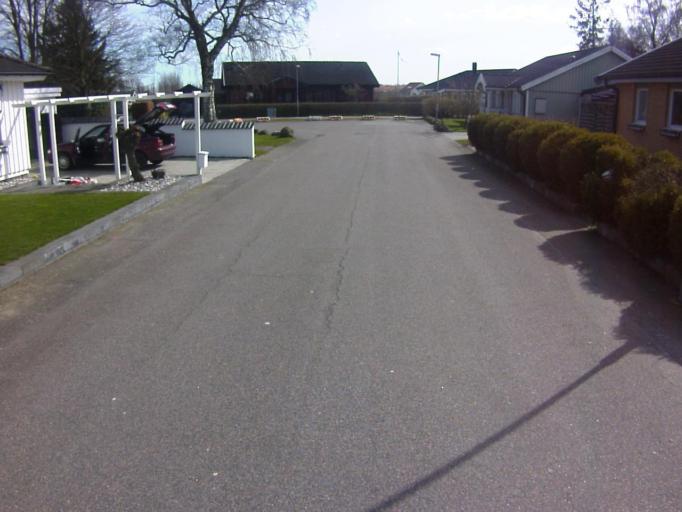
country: SE
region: Skane
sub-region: Kavlinge Kommun
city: Kaevlinge
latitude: 55.8048
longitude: 13.1141
